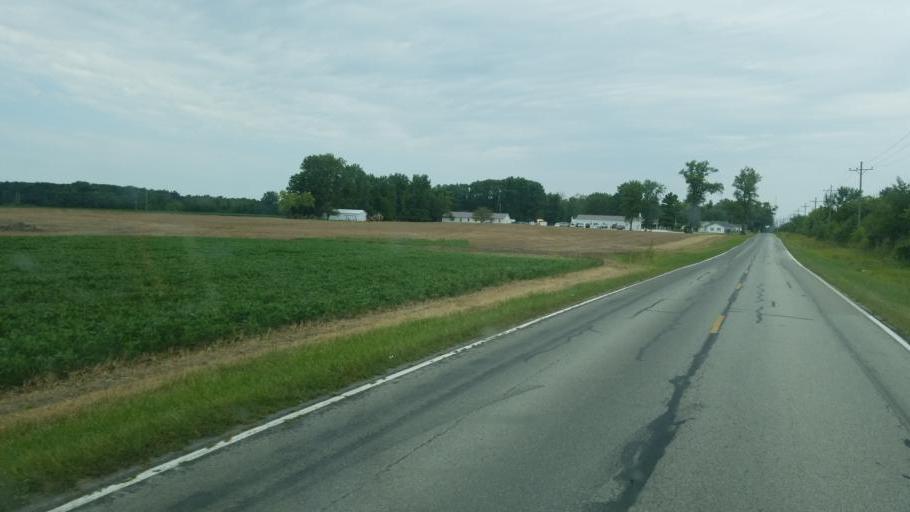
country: US
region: Ohio
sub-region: Marion County
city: Marion
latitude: 40.5509
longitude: -83.1491
